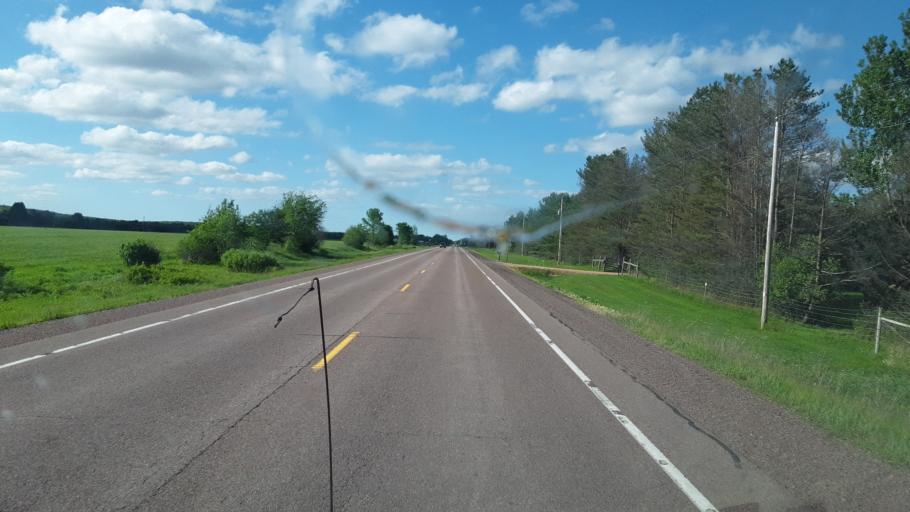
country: US
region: Wisconsin
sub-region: Wood County
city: Marshfield
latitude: 44.4788
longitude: -90.1806
